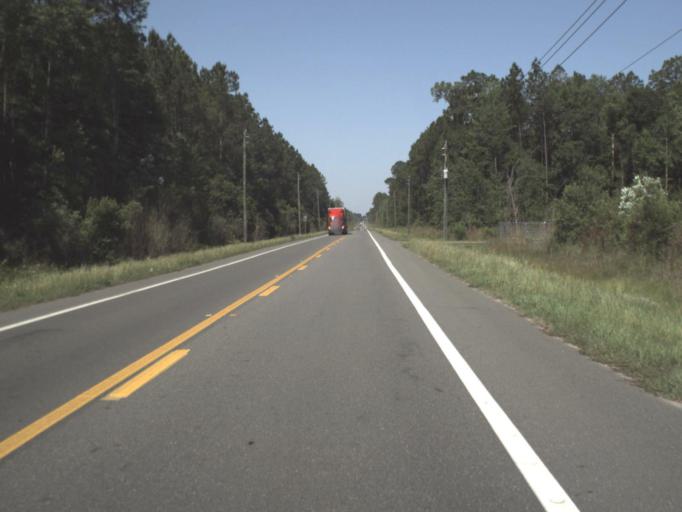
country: US
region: Florida
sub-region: Baker County
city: Macclenny
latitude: 30.2886
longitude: -82.0857
